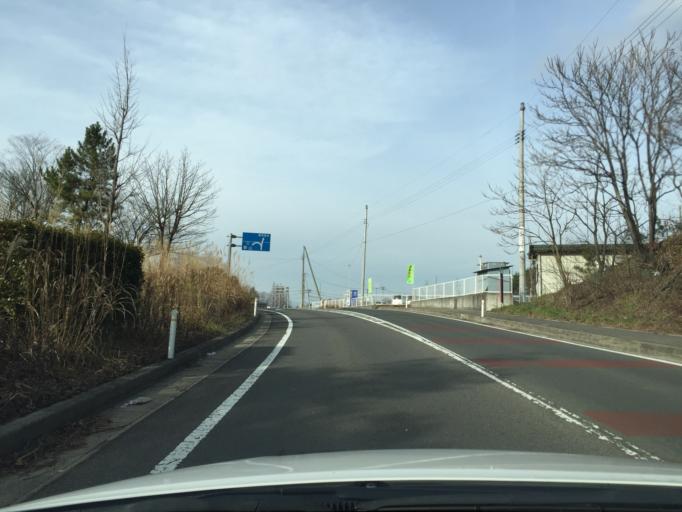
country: JP
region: Fukushima
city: Fukushima-shi
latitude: 37.6933
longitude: 140.4623
